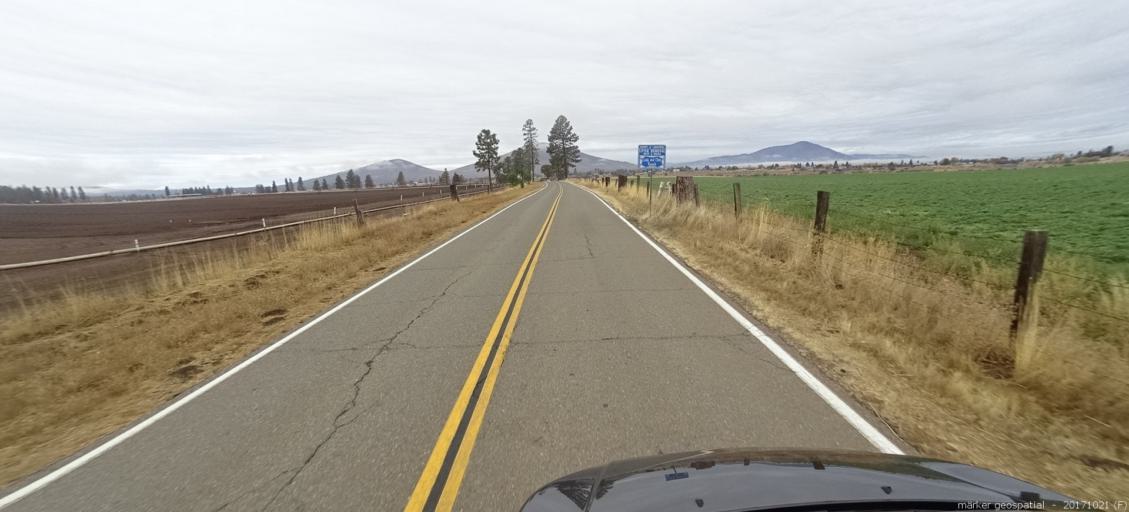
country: US
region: California
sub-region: Shasta County
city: Burney
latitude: 41.0256
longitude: -121.3982
